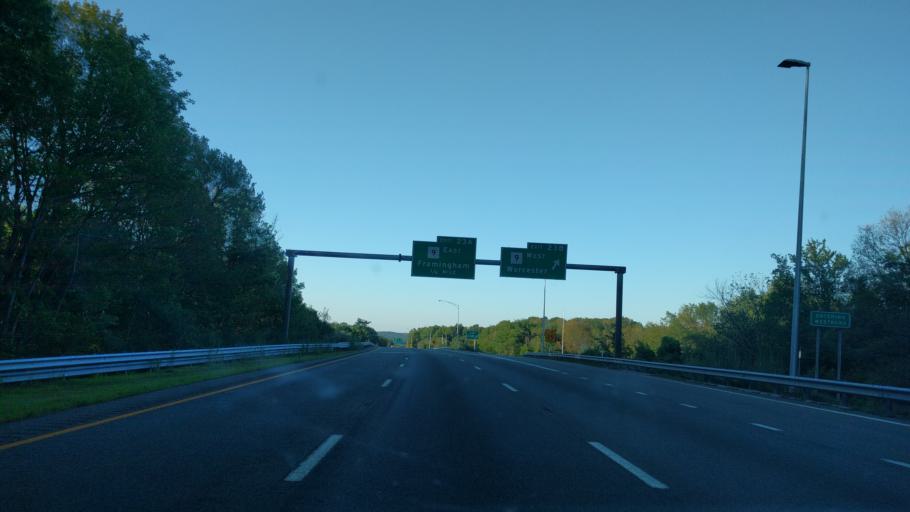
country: US
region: Massachusetts
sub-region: Worcester County
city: Southborough
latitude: 42.2927
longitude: -71.5682
